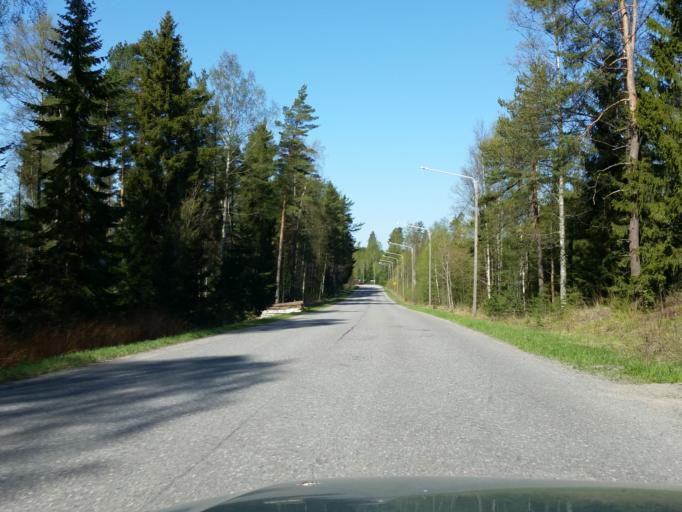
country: FI
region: Uusimaa
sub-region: Helsinki
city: Karjalohja
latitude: 60.1400
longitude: 23.8569
